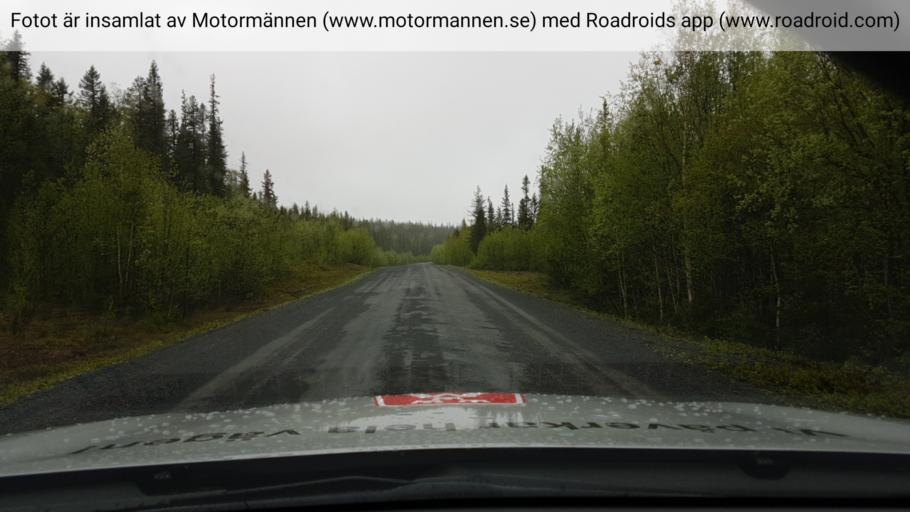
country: SE
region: Jaemtland
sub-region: Krokoms Kommun
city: Valla
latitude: 63.0990
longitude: 13.8839
